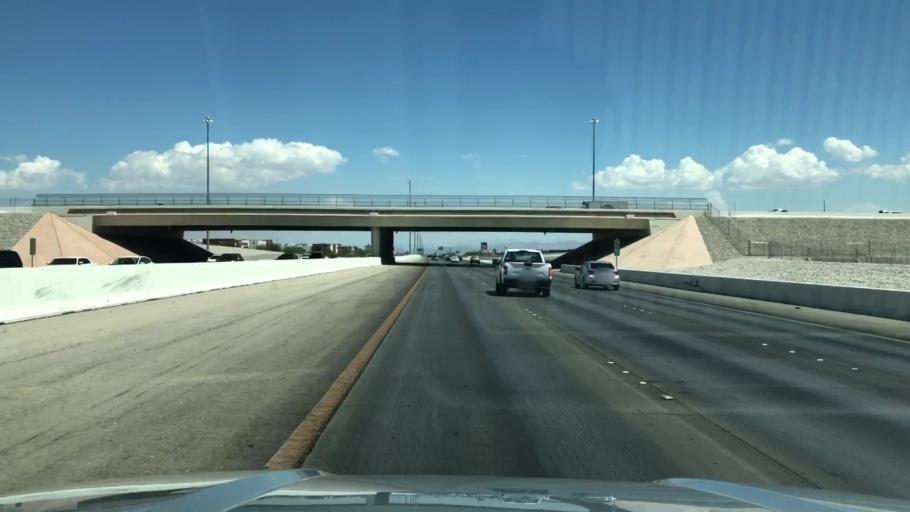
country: US
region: Nevada
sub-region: Clark County
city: Spring Valley
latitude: 36.0661
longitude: -115.2620
